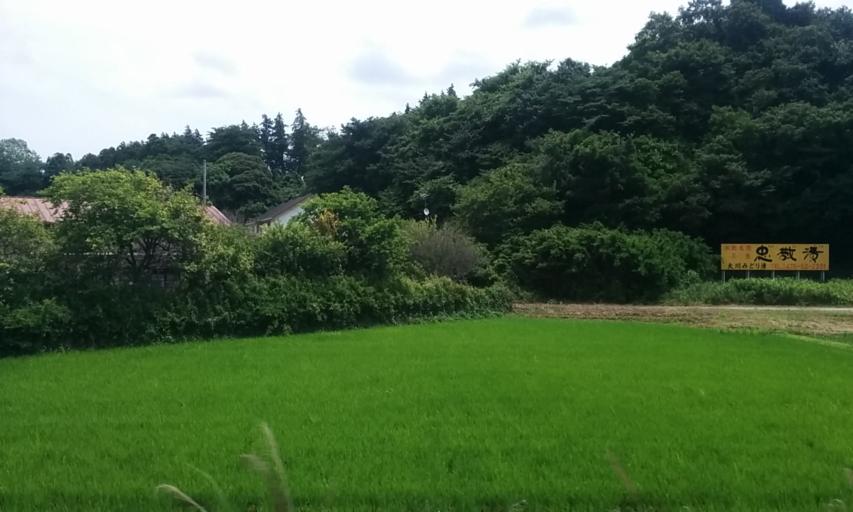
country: JP
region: Ibaraki
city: Edosaki
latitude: 35.8716
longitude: 140.3460
